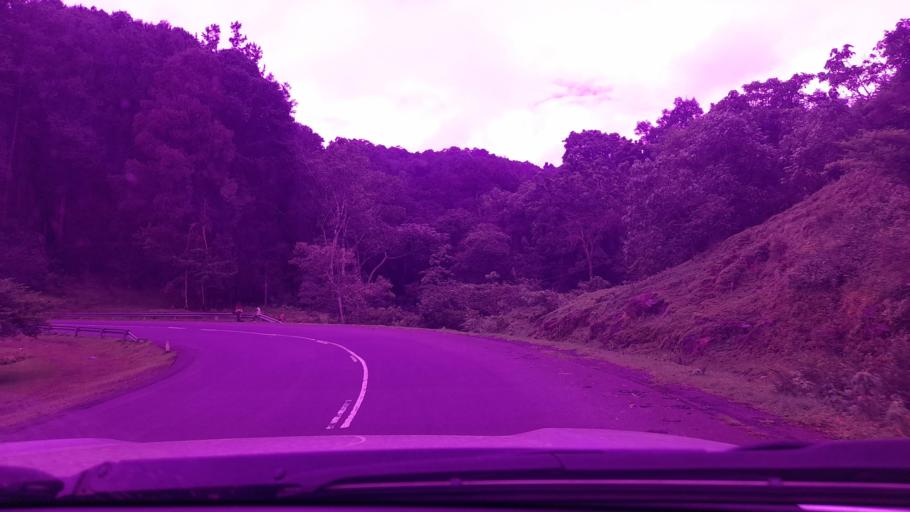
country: ET
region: Oromiya
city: Jima
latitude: 7.5564
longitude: 36.5874
